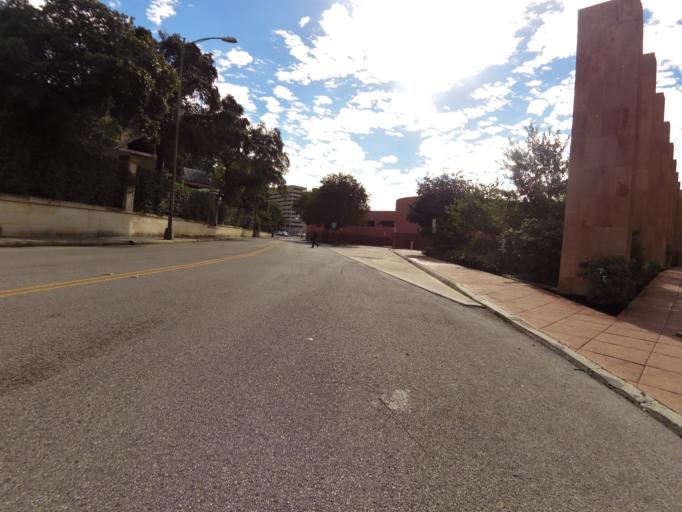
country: US
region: Texas
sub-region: Bexar County
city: San Antonio
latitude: 29.4321
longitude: -98.4920
